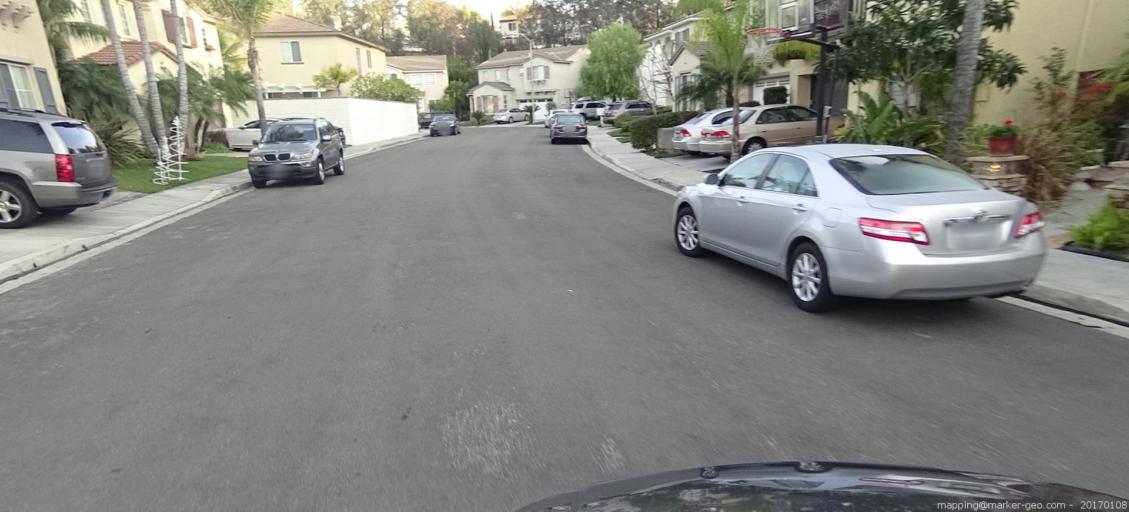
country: US
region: California
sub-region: Orange County
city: Las Flores
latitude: 33.5836
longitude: -117.6253
